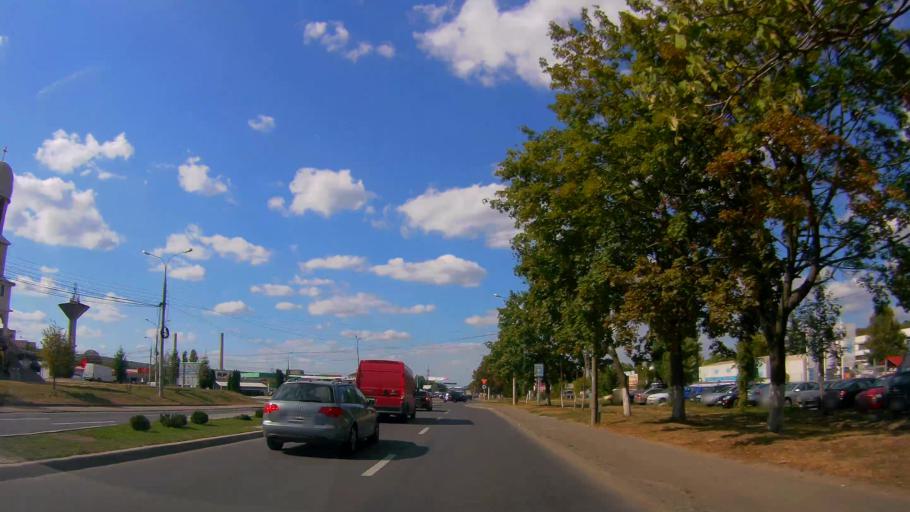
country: RO
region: Salaj
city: Zalau
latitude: 47.2025
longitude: 23.0527
